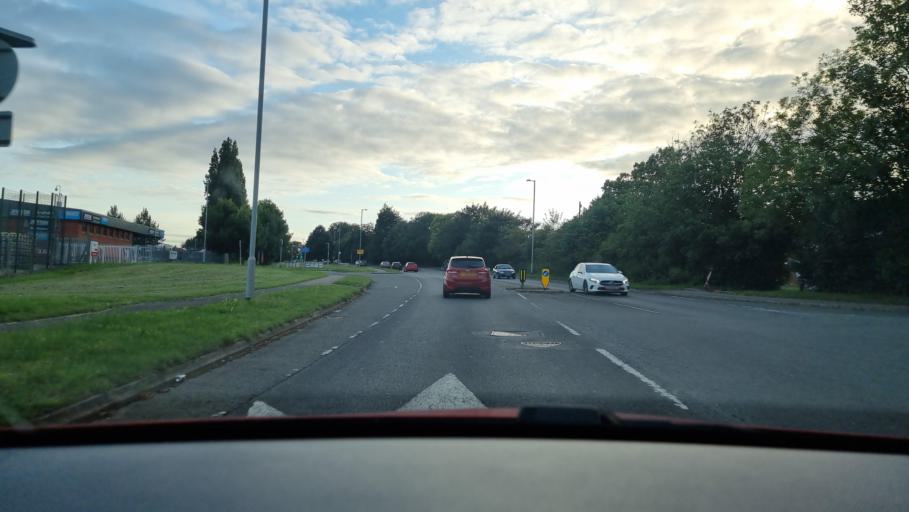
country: GB
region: England
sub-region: Northamptonshire
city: Northampton
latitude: 52.2566
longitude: -0.9135
